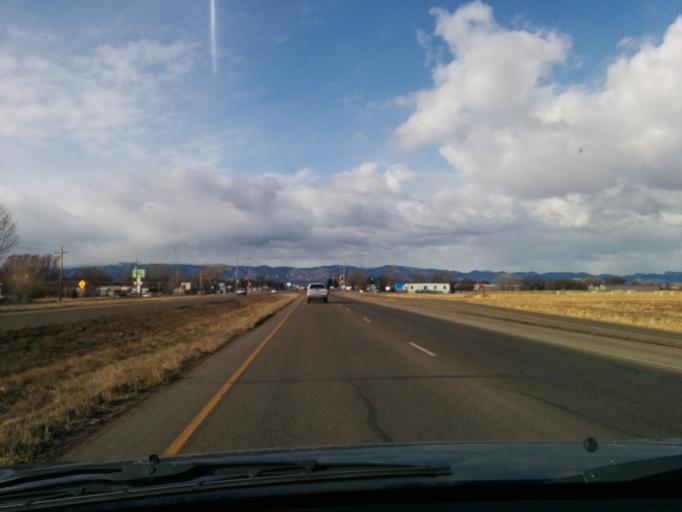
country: US
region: Colorado
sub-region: Larimer County
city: Fort Collins
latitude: 40.5812
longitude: -105.0122
